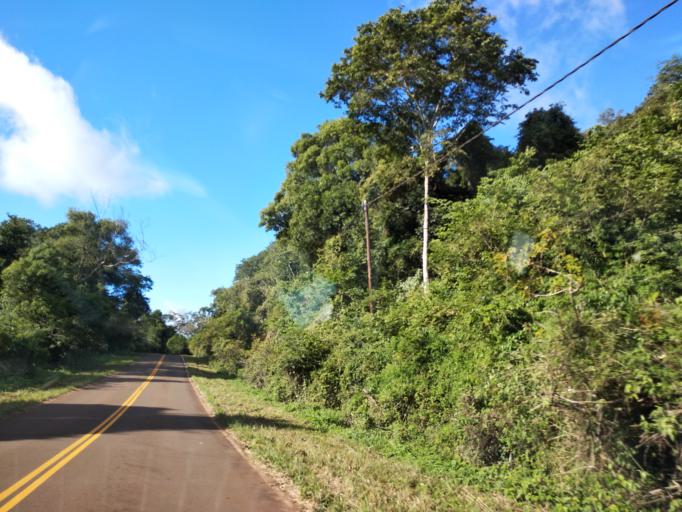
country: AR
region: Misiones
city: Cerro Cora
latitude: -27.4487
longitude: -55.5674
